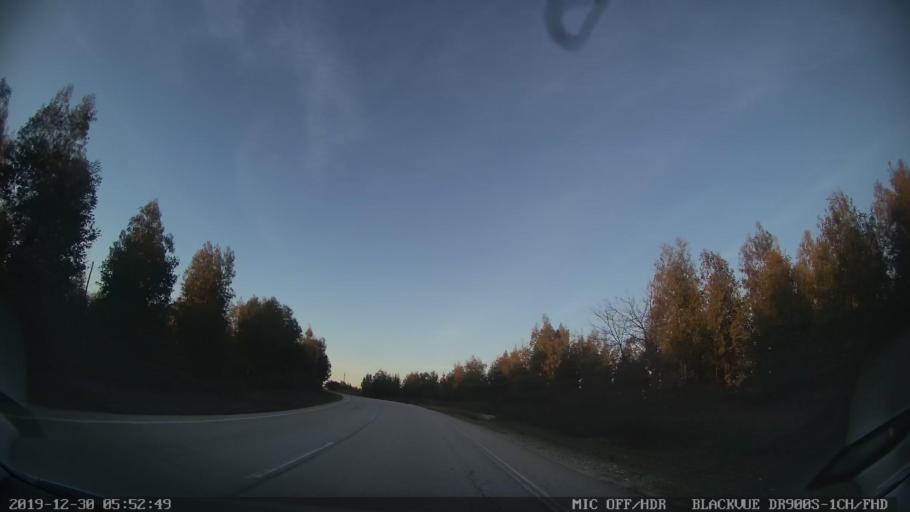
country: PT
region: Castelo Branco
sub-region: Idanha-A-Nova
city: Idanha-a-Nova
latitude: 40.0091
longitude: -7.2488
